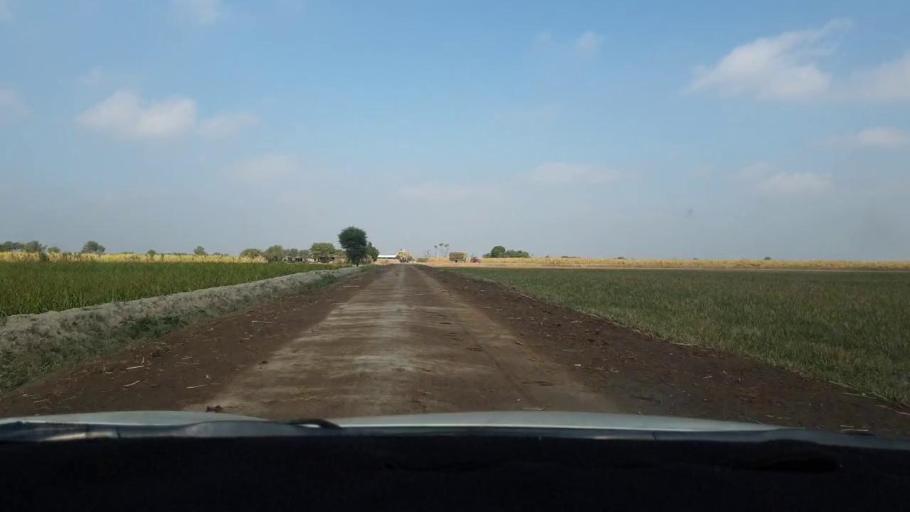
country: PK
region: Sindh
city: Berani
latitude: 25.7491
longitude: 69.0076
